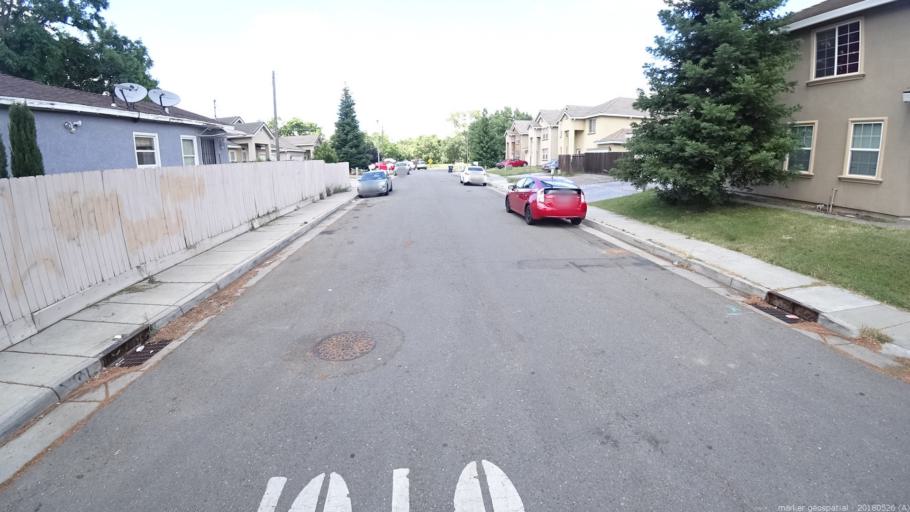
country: US
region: California
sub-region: Sacramento County
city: Sacramento
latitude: 38.6122
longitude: -121.4746
